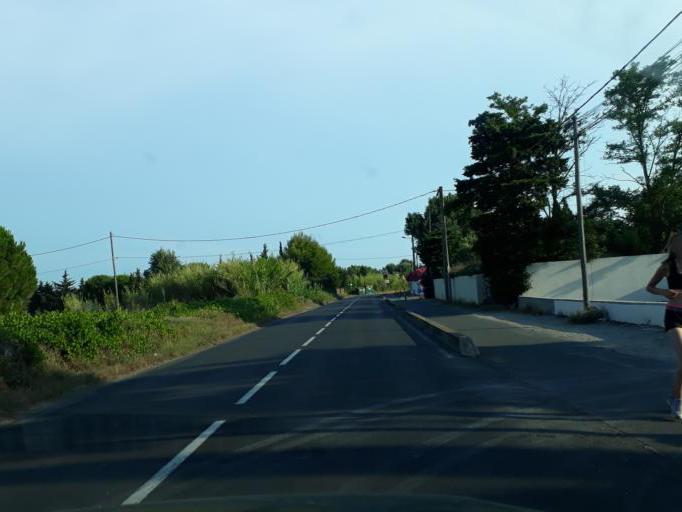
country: FR
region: Languedoc-Roussillon
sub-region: Departement de l'Herault
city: Agde
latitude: 43.2821
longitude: 3.4817
